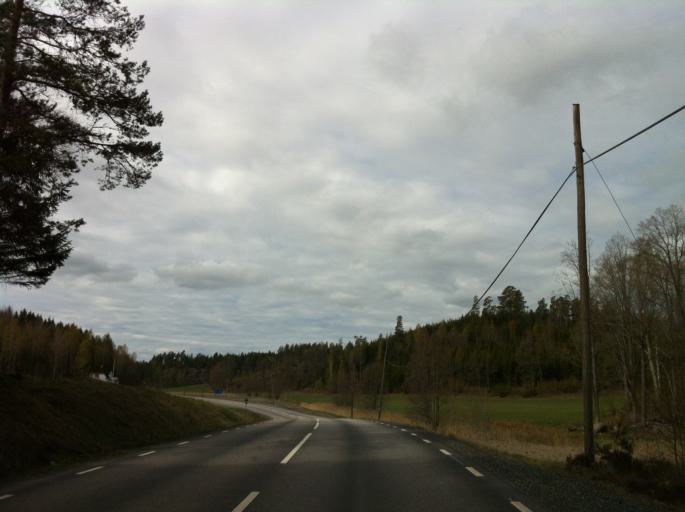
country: SE
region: OEstergoetland
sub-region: Valdemarsviks Kommun
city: Valdemarsvik
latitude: 58.1884
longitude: 16.6431
